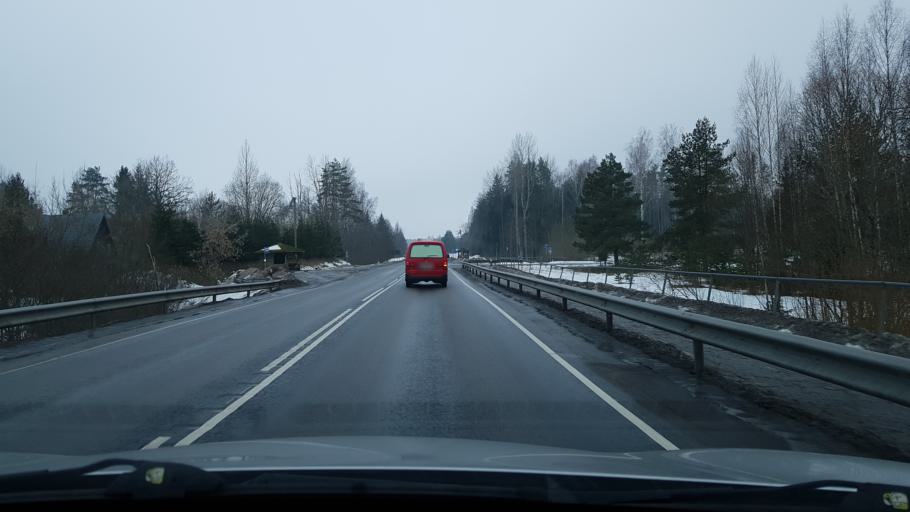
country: EE
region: Valgamaa
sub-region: Valga linn
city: Valga
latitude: 57.8502
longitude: 26.1326
